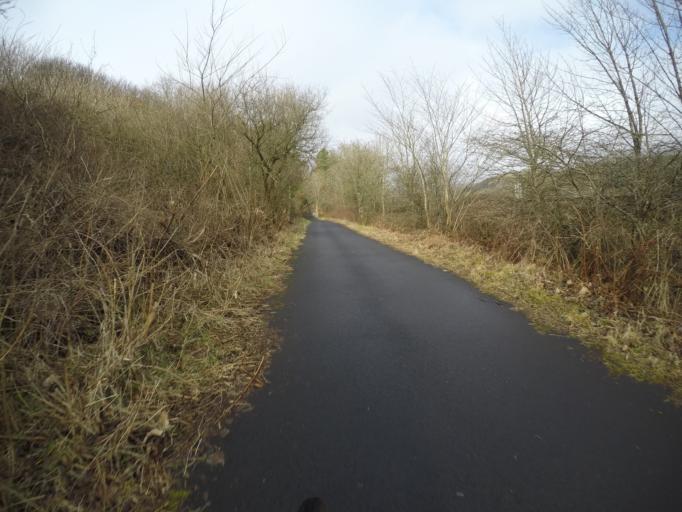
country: GB
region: Scotland
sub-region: North Ayrshire
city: Fairlie
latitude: 55.7381
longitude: -4.8616
